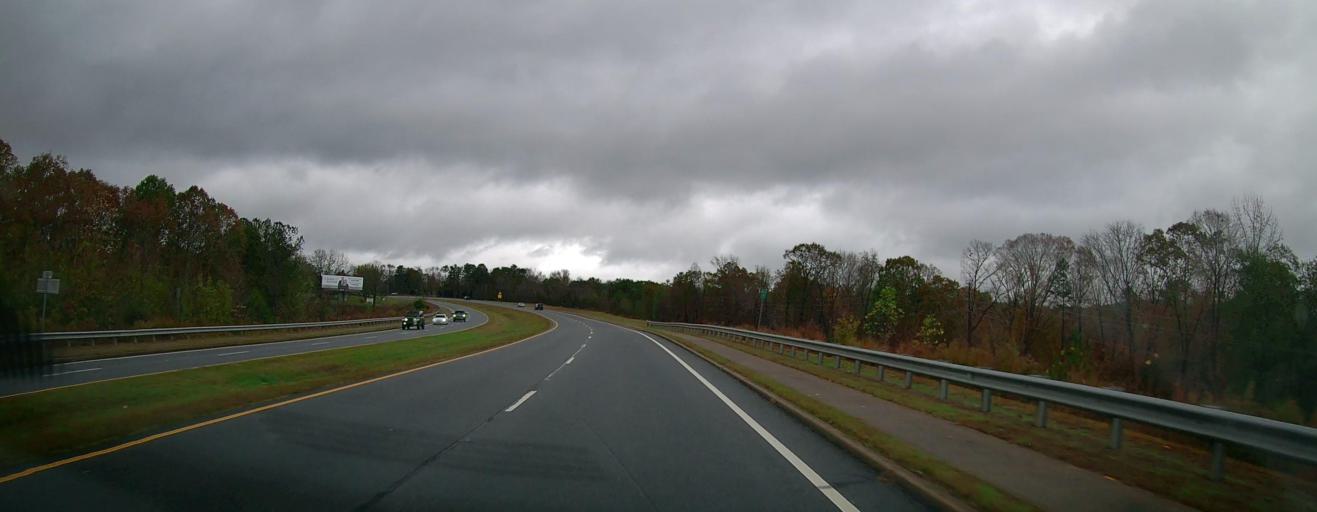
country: US
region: Georgia
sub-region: Jackson County
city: Nicholson
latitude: 34.1279
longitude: -83.4284
